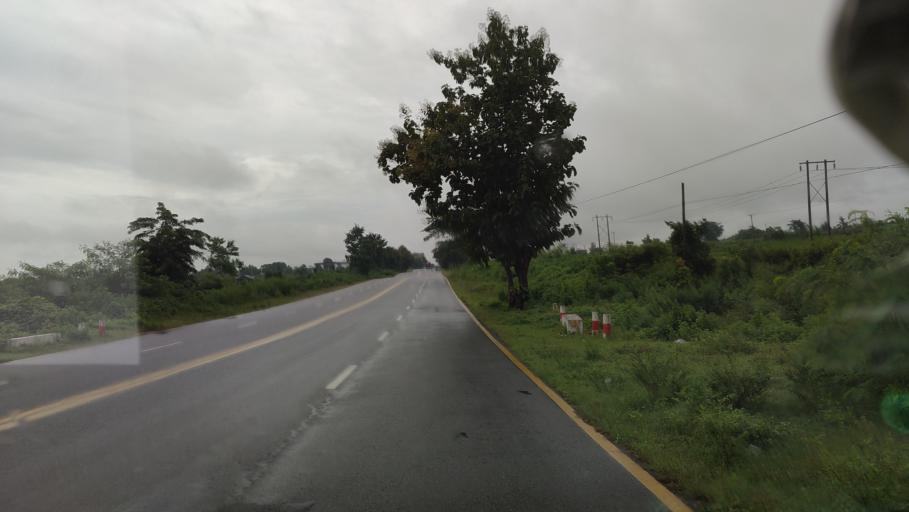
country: MM
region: Mandalay
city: Pyinmana
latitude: 19.9413
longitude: 96.2524
